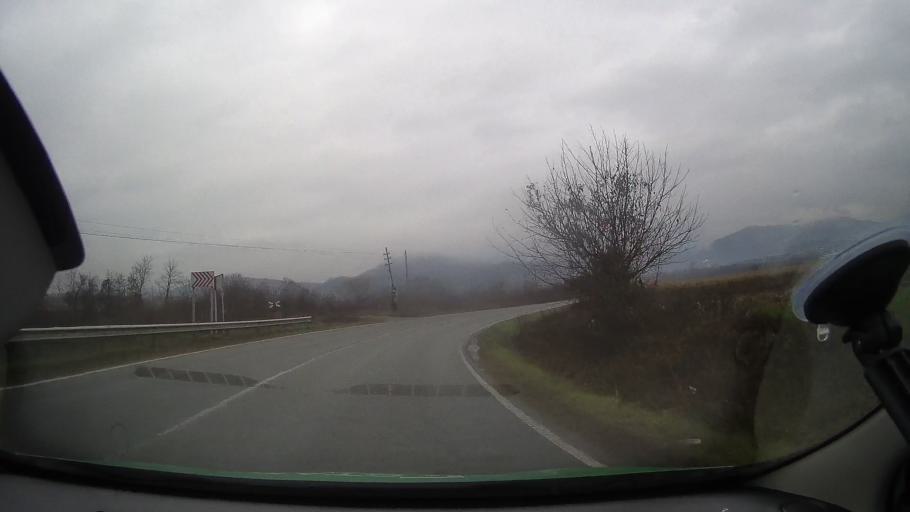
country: RO
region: Arad
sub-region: Comuna Gurahont
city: Gurahont
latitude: 46.2747
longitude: 22.3273
